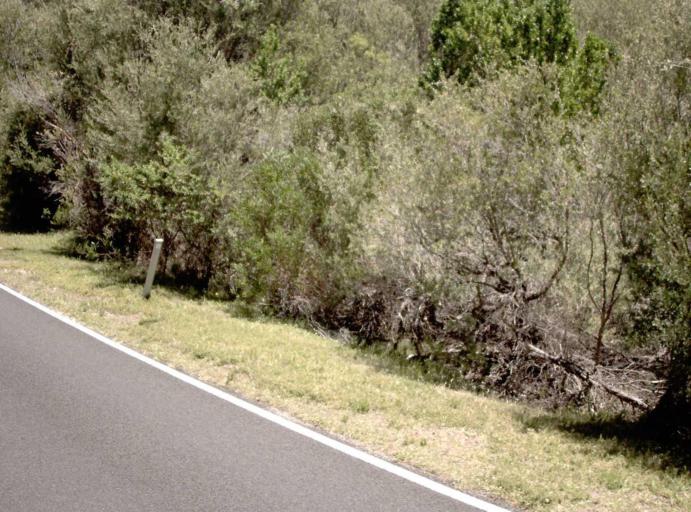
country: AU
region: Victoria
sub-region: Latrobe
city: Morwell
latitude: -38.8811
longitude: 146.2642
